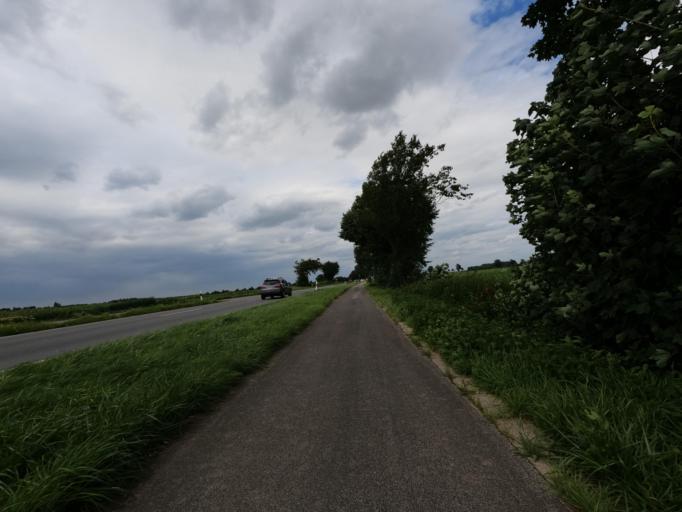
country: DE
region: North Rhine-Westphalia
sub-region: Regierungsbezirk Koln
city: Ubach-Palenberg
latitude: 50.9361
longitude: 6.1331
